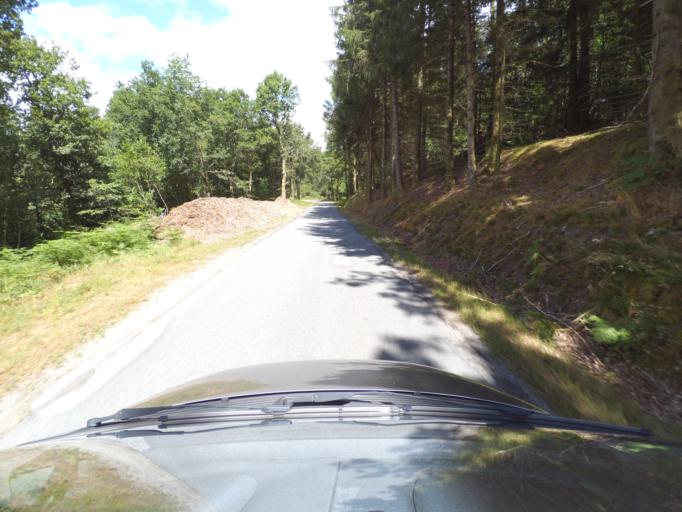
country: FR
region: Limousin
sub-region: Departement de la Creuse
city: Banize
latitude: 45.7905
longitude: 1.9340
